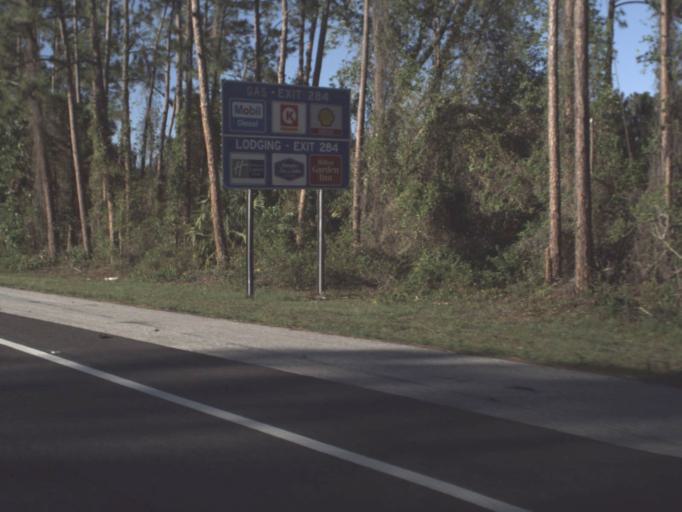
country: US
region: Florida
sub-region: Flagler County
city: Flagler Beach
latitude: 29.4661
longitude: -81.1799
